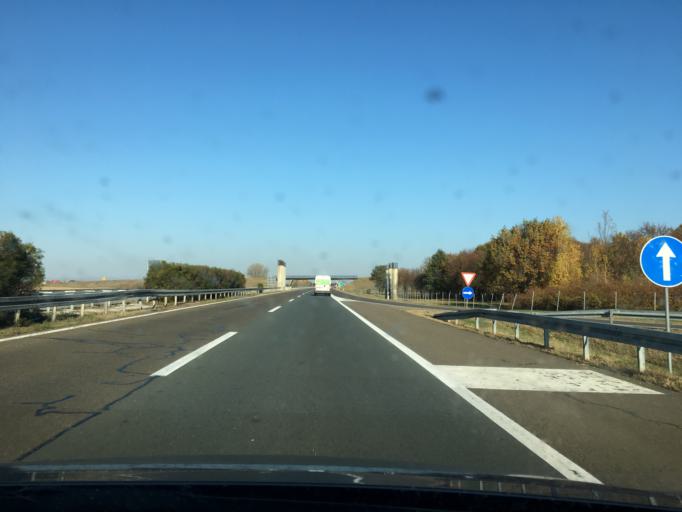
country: RS
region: Autonomna Pokrajina Vojvodina
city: Nova Pazova
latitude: 44.9838
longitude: 20.2180
